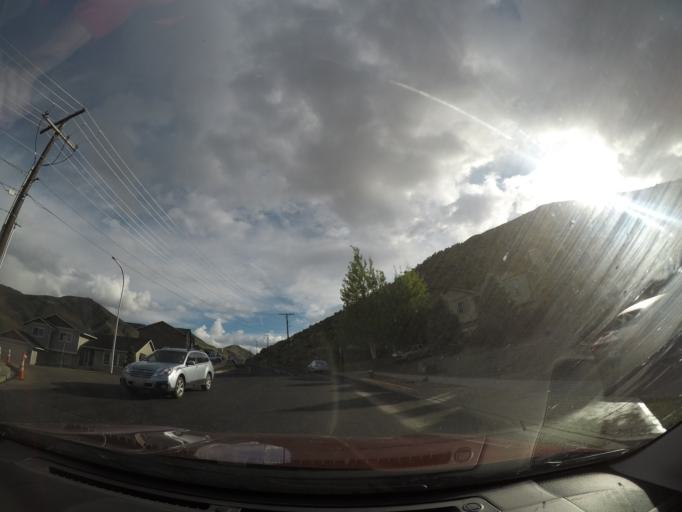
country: US
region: Washington
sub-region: Chelan County
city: South Wenatchee
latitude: 47.3903
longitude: -120.3098
